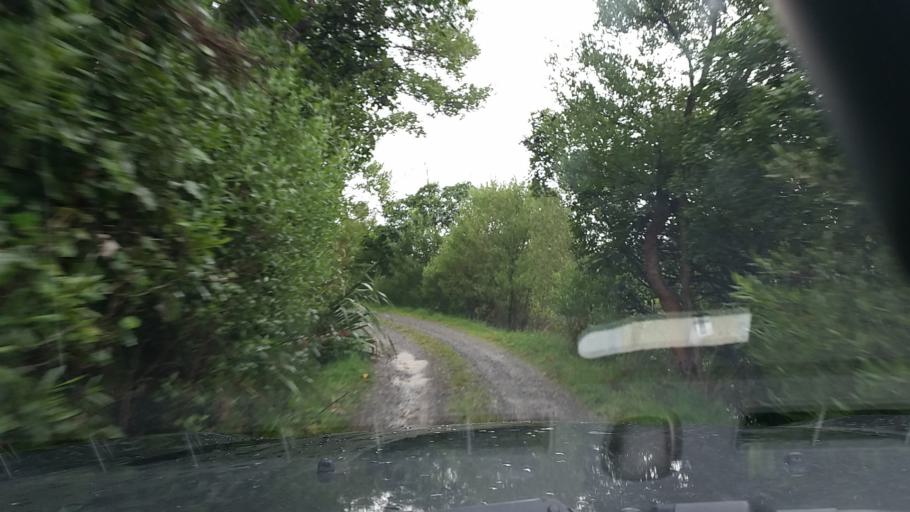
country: NZ
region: Marlborough
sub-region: Marlborough District
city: Picton
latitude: -41.2652
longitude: 174.0366
